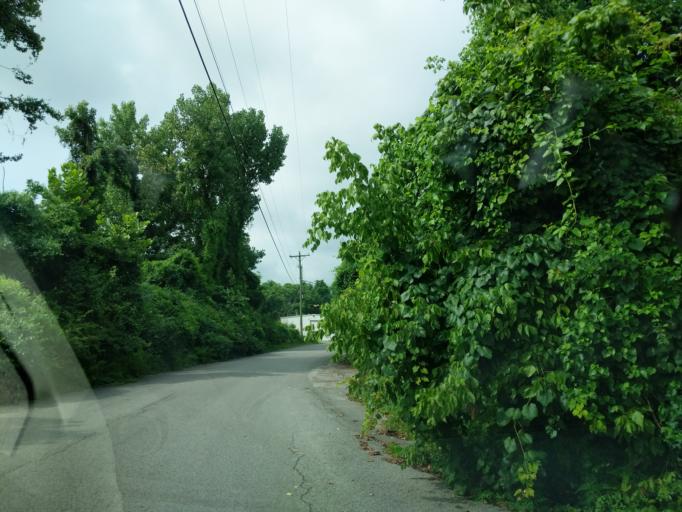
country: US
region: Tennessee
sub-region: Davidson County
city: Lakewood
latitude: 36.1883
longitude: -86.6243
